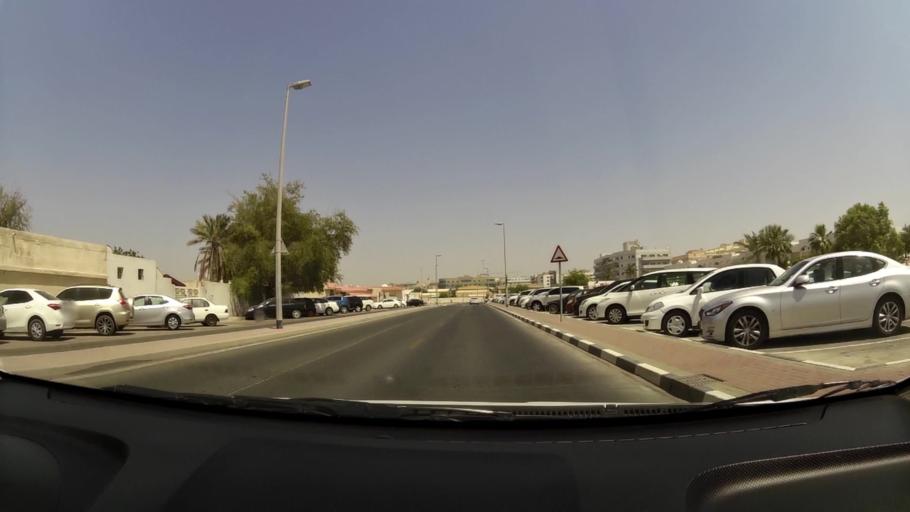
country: AE
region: Ash Shariqah
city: Sharjah
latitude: 25.2824
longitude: 55.3441
